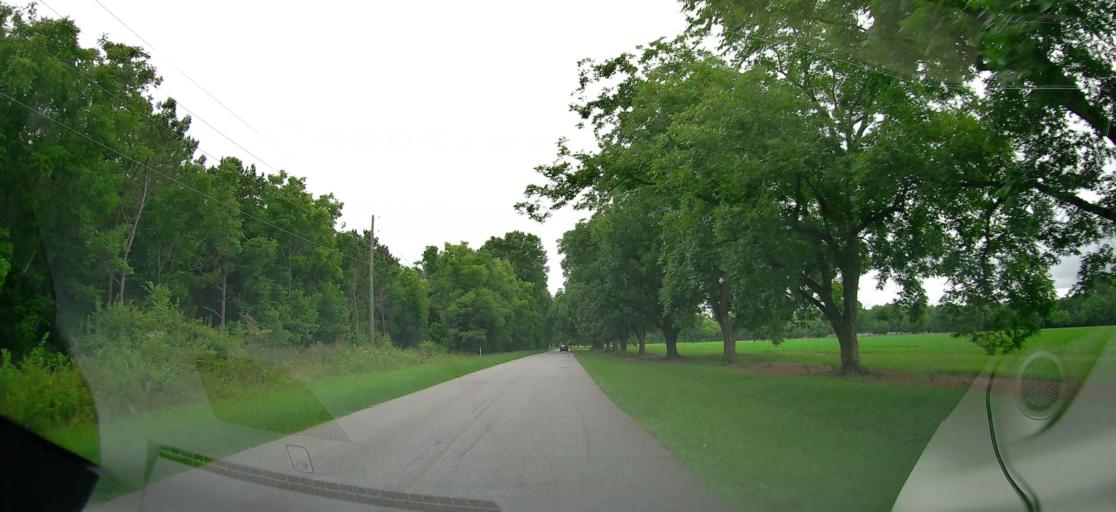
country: US
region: Georgia
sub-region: Peach County
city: Byron
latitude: 32.6361
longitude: -83.7412
